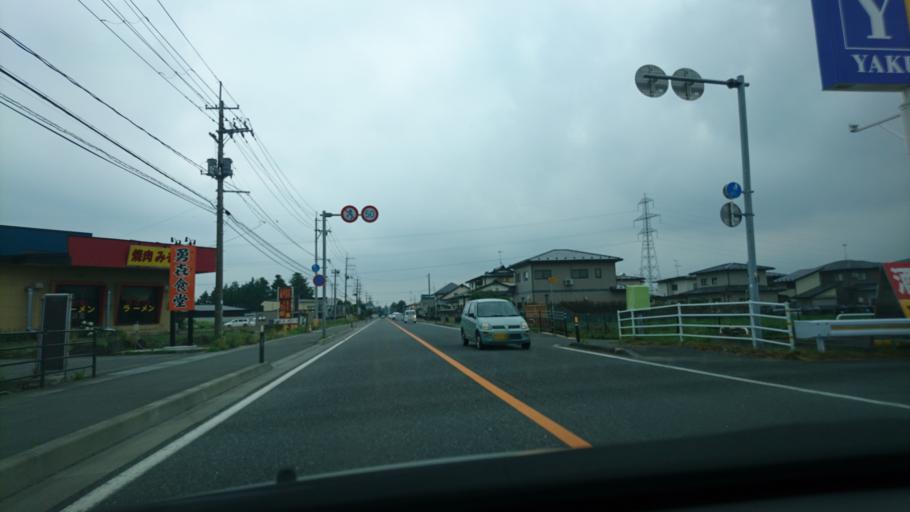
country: JP
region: Miyagi
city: Furukawa
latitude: 38.6418
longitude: 140.8823
